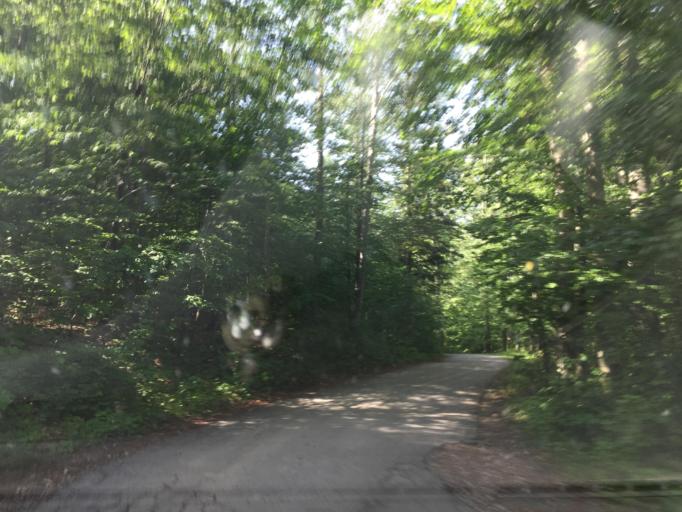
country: HR
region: Primorsko-Goranska
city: Podhum
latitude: 45.4357
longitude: 14.5632
